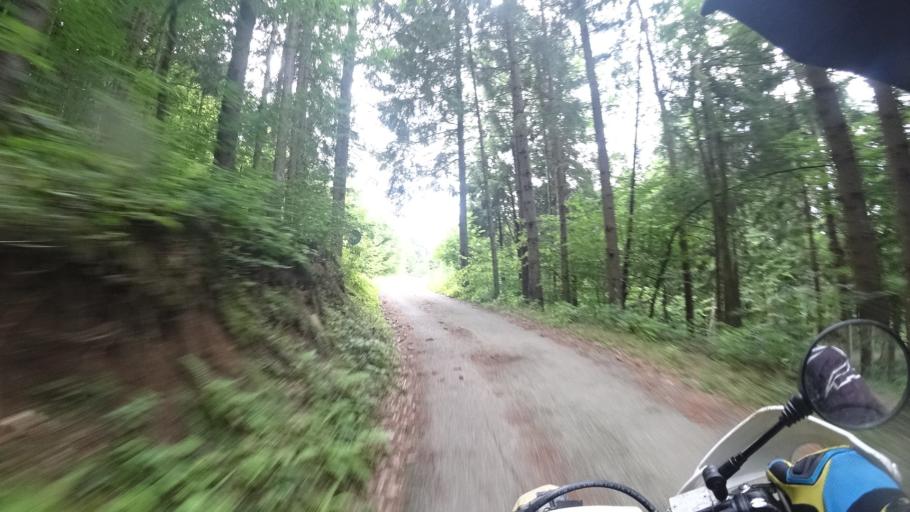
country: SI
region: Osilnica
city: Osilnica
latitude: 45.4870
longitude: 14.7033
